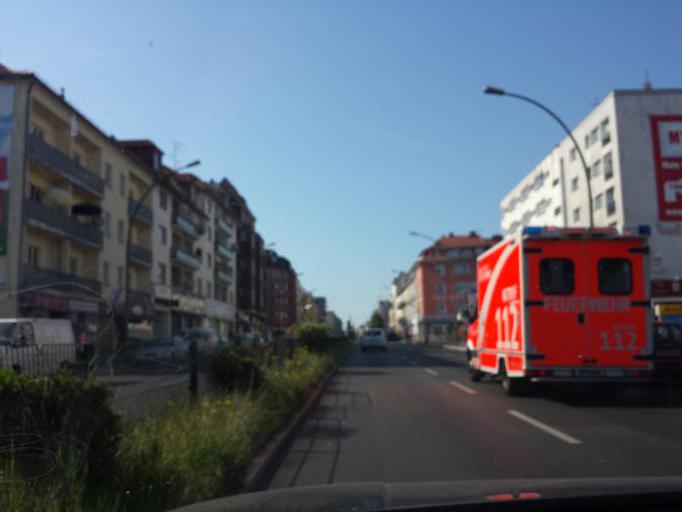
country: DE
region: Berlin
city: Mariendorf
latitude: 52.4489
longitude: 13.3851
